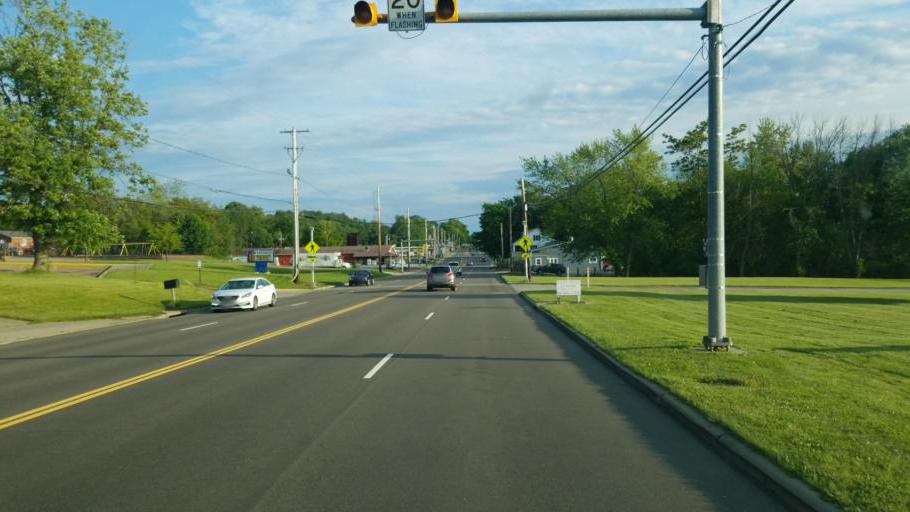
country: US
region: Ohio
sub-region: Stark County
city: Uniontown
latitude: 40.9795
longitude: -81.4069
